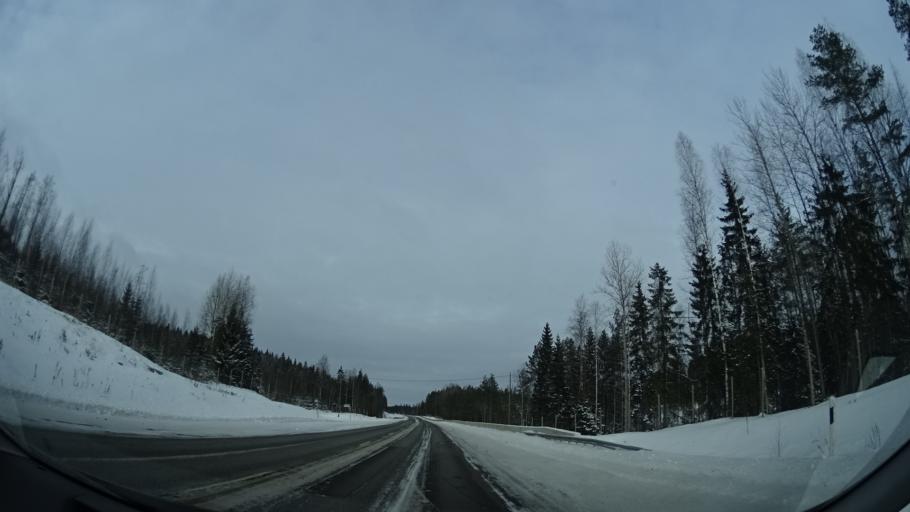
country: FI
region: Uusimaa
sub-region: Helsinki
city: Kaerkoelae
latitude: 60.6018
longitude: 24.0815
